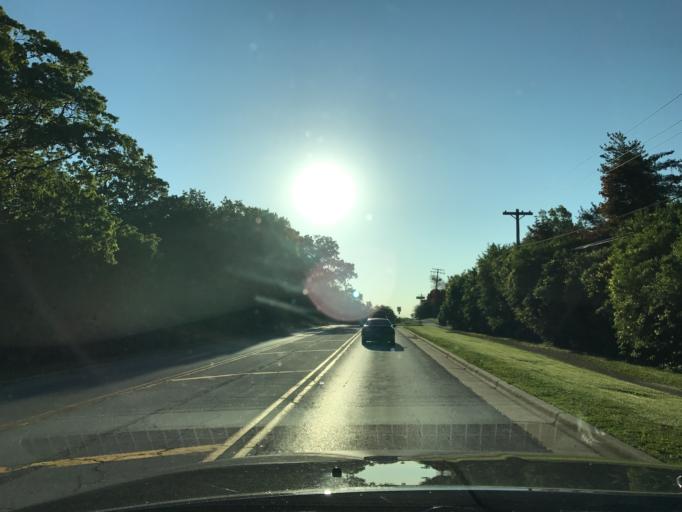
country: US
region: Illinois
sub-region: DuPage County
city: Woodridge
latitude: 41.7564
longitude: -88.0976
